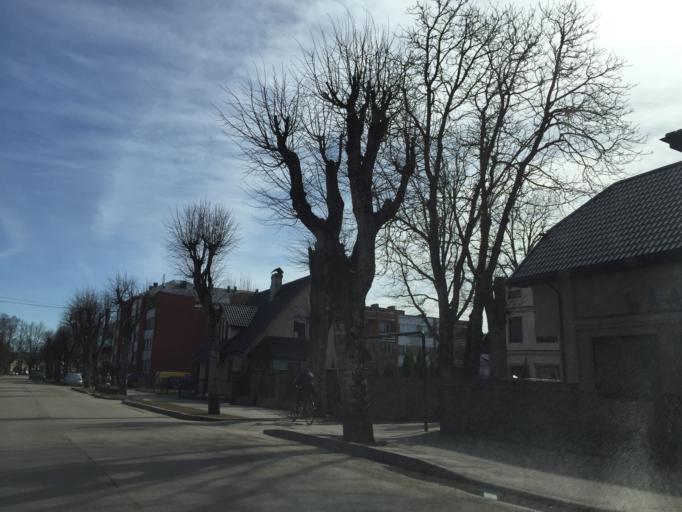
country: LV
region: Sigulda
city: Sigulda
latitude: 57.1586
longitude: 24.8484
